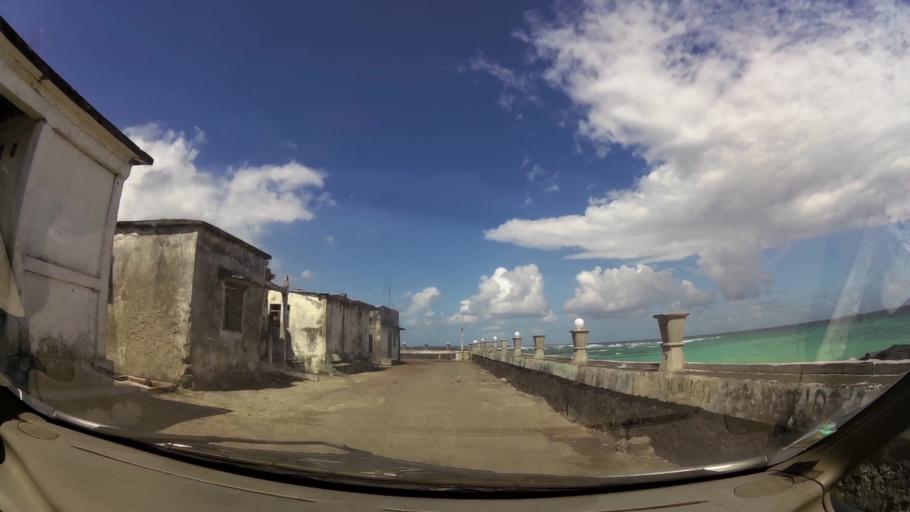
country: KM
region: Grande Comore
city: Mavingouni
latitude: -11.7459
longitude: 43.2313
